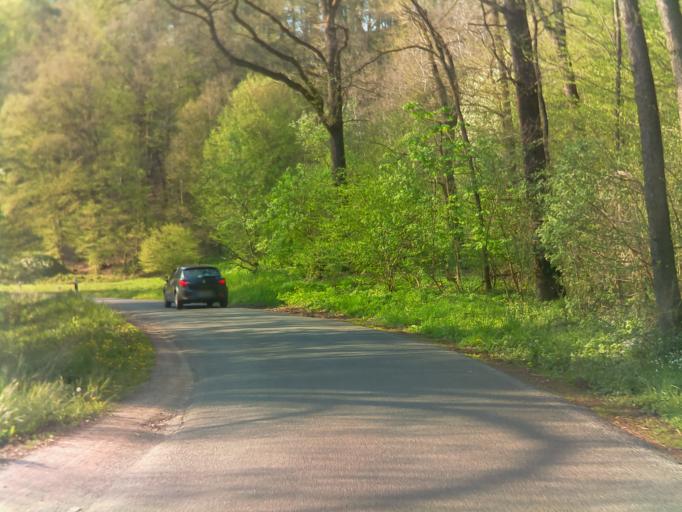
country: DE
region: Thuringia
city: Orlamunde
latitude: 50.7519
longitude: 11.5224
